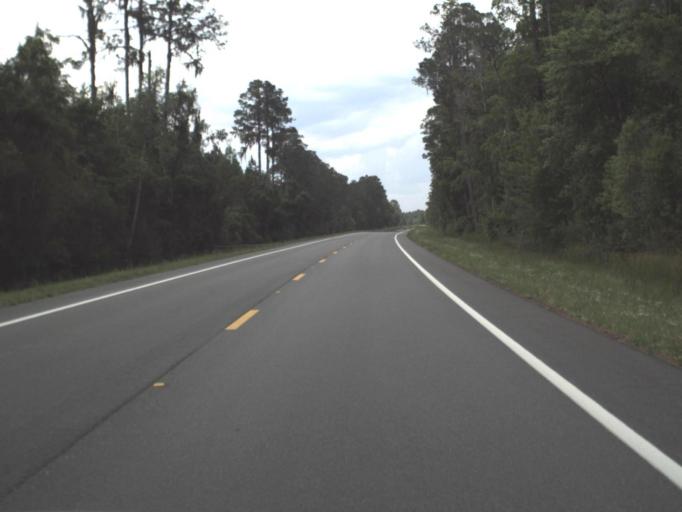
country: US
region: Florida
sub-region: Hamilton County
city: Jasper
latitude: 30.5394
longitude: -82.6785
